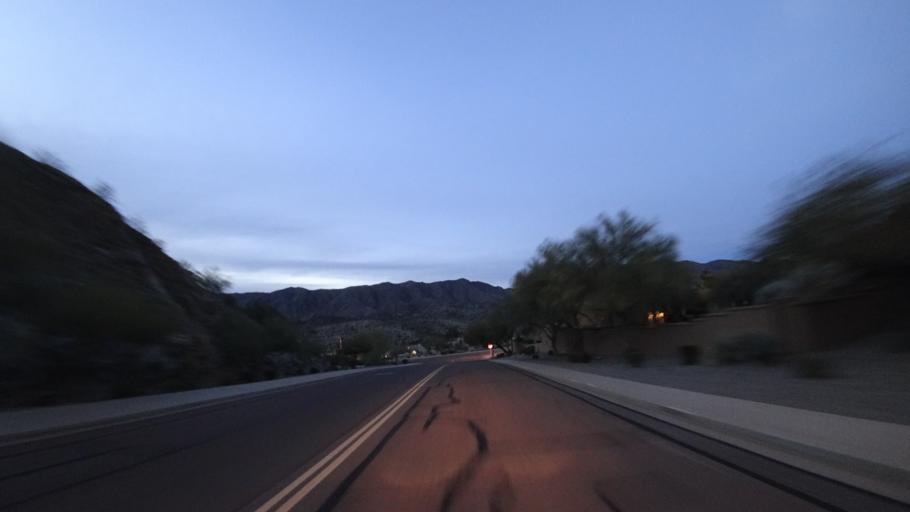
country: US
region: Arizona
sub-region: Maricopa County
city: Laveen
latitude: 33.3036
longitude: -112.0704
